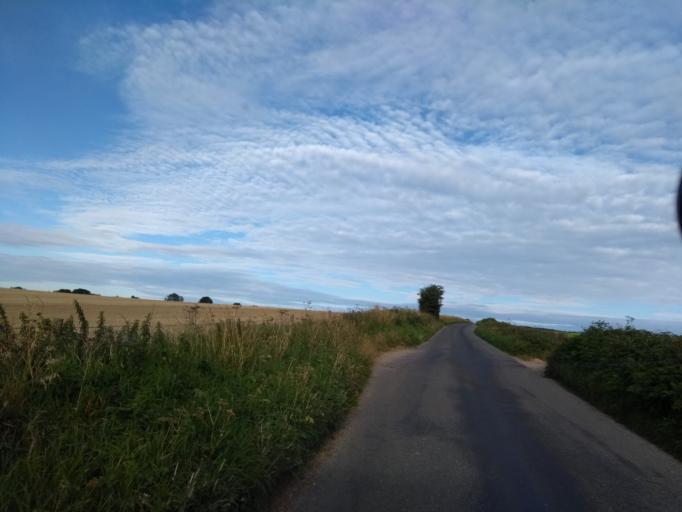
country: GB
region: England
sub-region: Dorset
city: Beaminster
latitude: 50.8277
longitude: -2.7152
